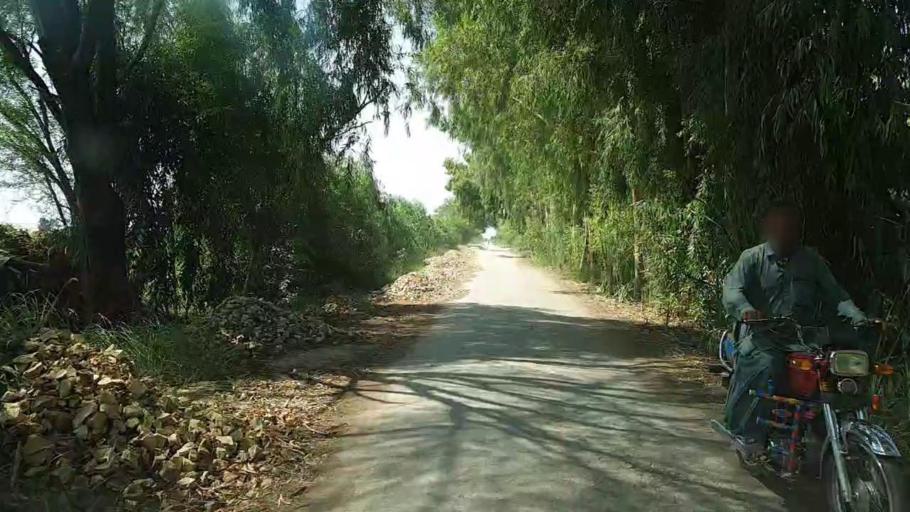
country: PK
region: Sindh
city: Khairpur
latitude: 28.0878
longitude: 69.6325
